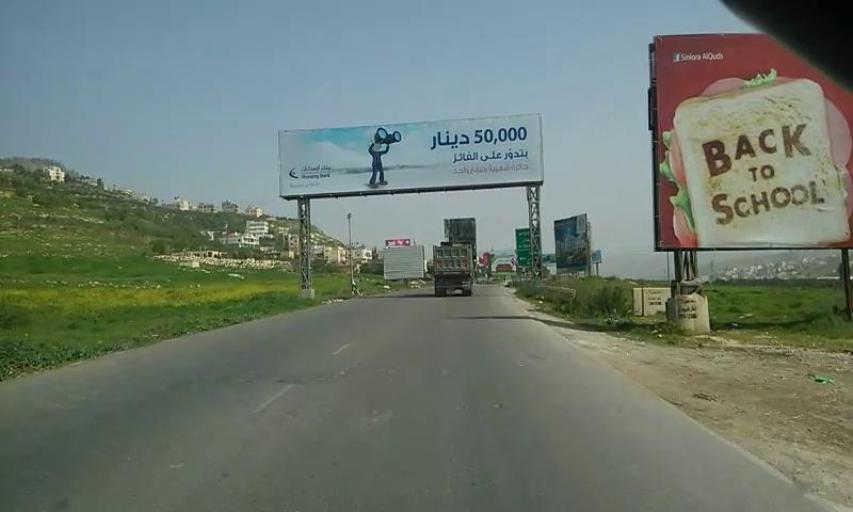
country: PS
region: West Bank
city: Kafr Qallil
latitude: 32.1803
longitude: 35.2749
